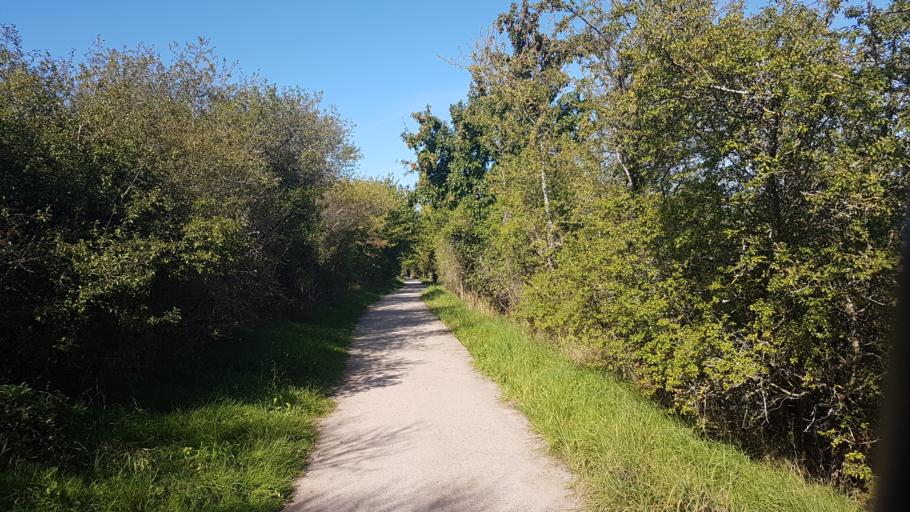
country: DE
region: Mecklenburg-Vorpommern
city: Glowe
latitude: 54.5579
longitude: 13.4947
